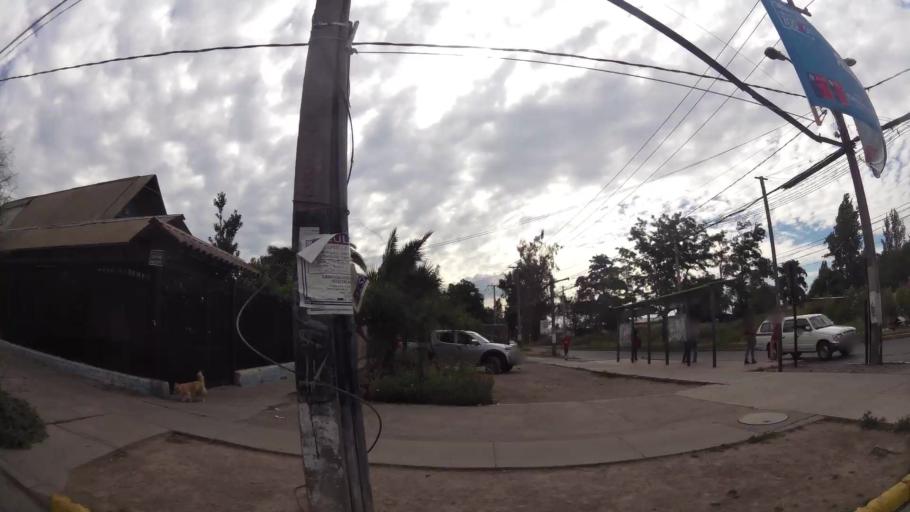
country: CL
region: Santiago Metropolitan
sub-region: Provincia de Santiago
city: La Pintana
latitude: -33.6178
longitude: -70.6195
